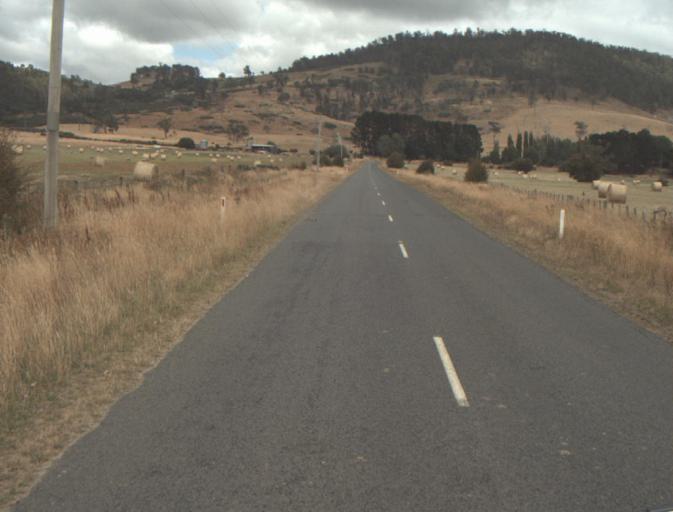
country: AU
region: Tasmania
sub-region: Northern Midlands
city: Evandale
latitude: -41.5019
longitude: 147.4882
